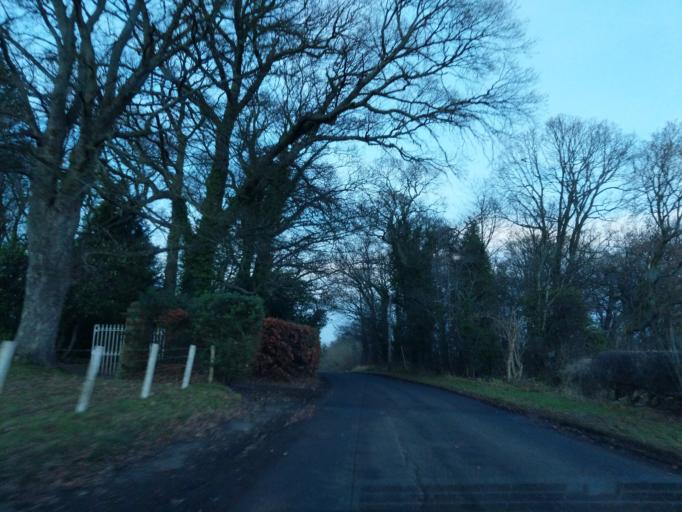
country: GB
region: Scotland
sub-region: Midlothian
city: Bonnyrigg
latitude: 55.8569
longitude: -3.0984
